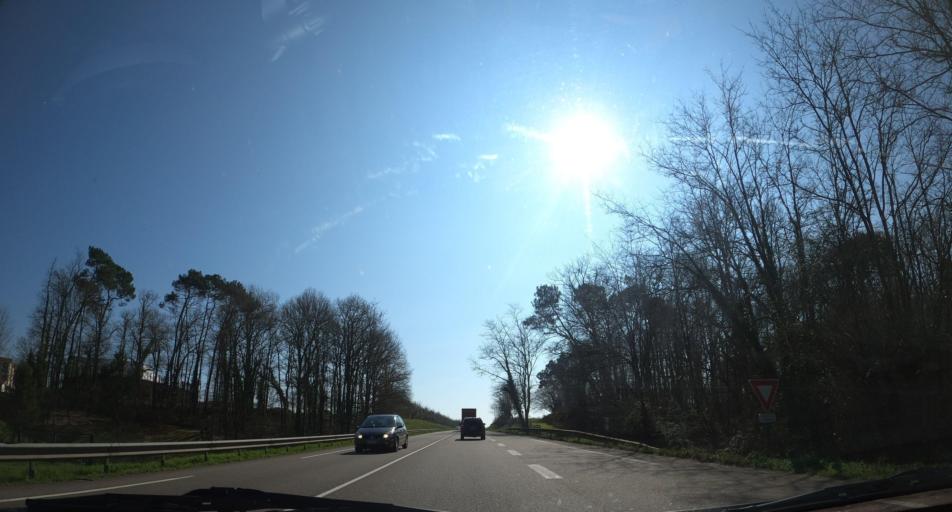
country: FR
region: Aquitaine
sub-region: Departement des Landes
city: Saint-Pierre-du-Mont
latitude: 43.8808
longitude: -0.5261
